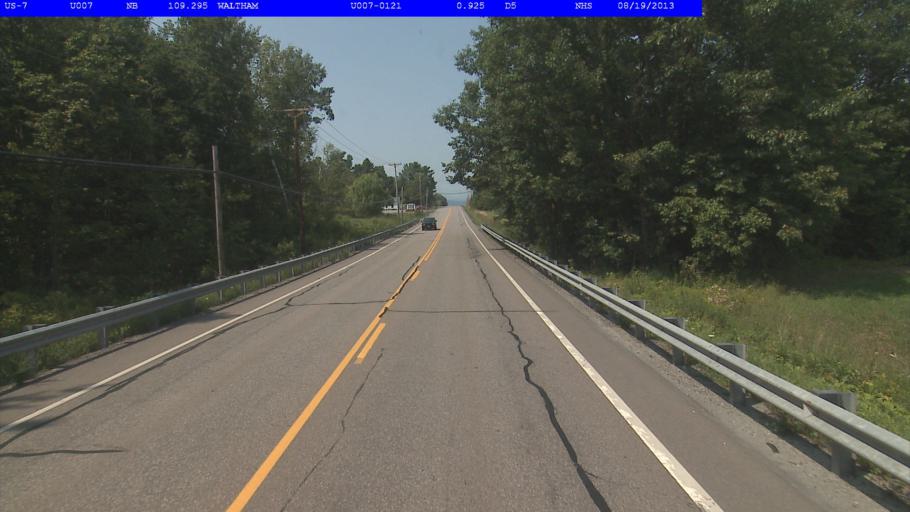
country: US
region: Vermont
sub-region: Addison County
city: Vergennes
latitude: 44.1573
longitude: -73.2230
